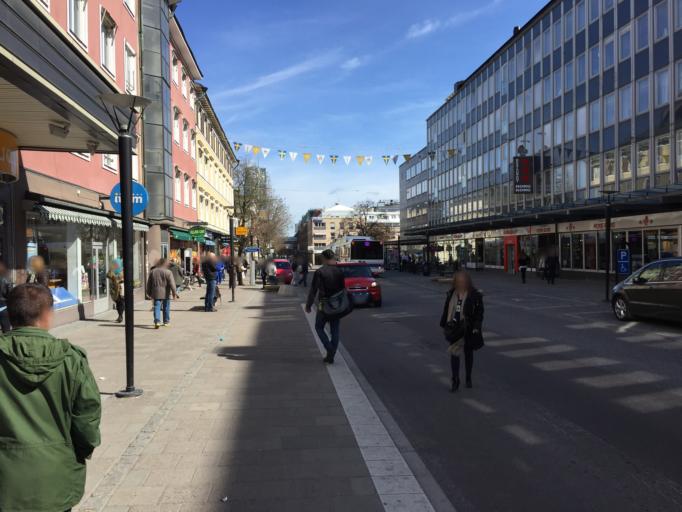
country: SE
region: Vaestmanland
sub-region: Vasteras
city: Vasteras
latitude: 59.6087
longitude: 16.5415
